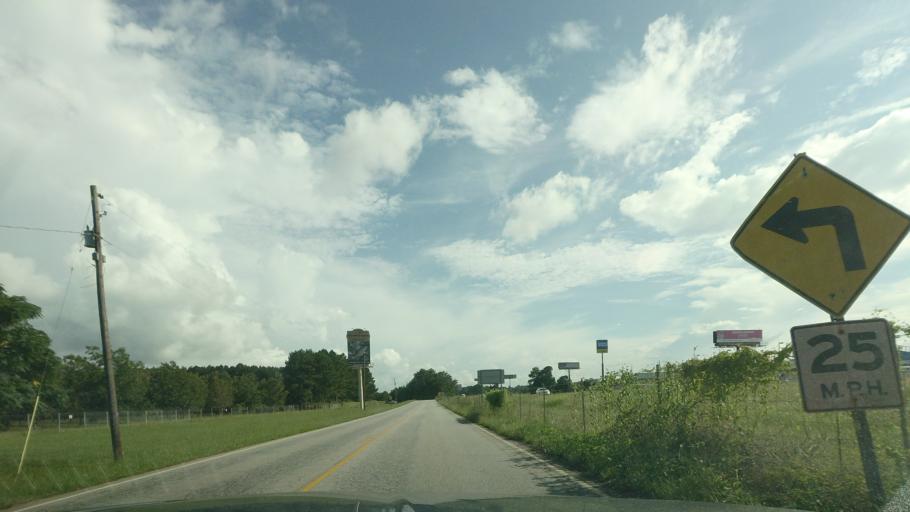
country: US
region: Georgia
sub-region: Peach County
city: Byron
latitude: 32.6540
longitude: -83.7437
